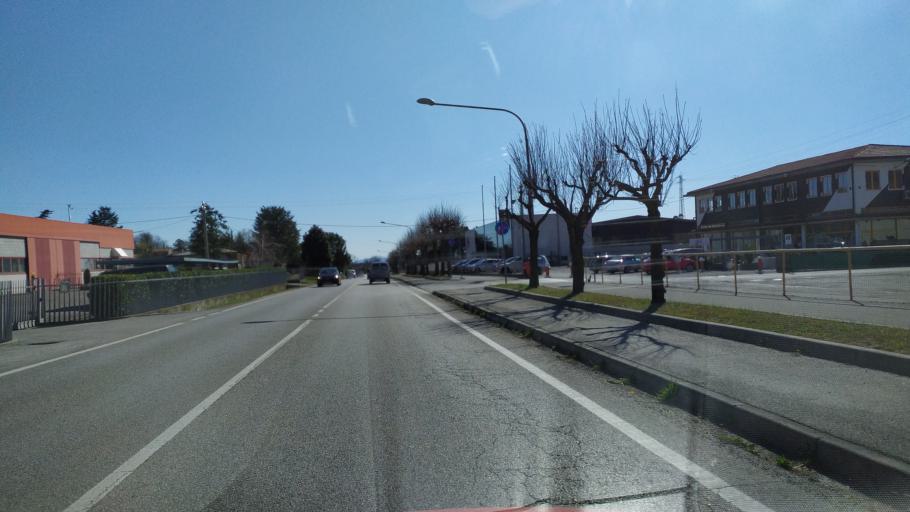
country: IT
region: Veneto
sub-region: Provincia di Vicenza
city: Carre
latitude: 45.7411
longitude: 11.4628
